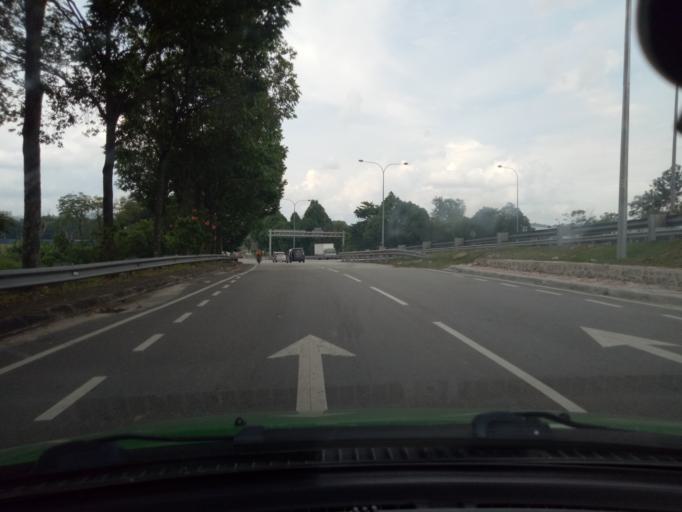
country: MY
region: Selangor
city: Kampong Baharu Balakong
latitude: 3.0041
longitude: 101.7835
